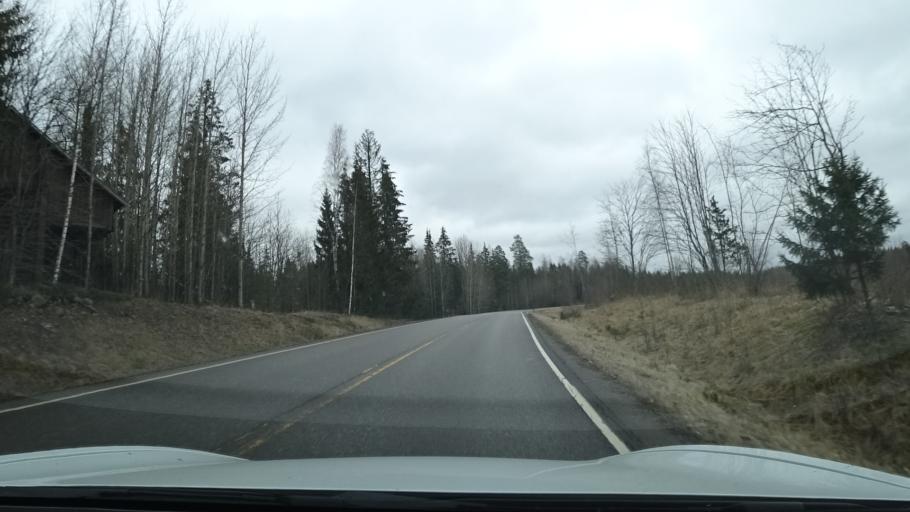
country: FI
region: Uusimaa
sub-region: Helsinki
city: Pornainen
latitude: 60.4902
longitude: 25.4583
